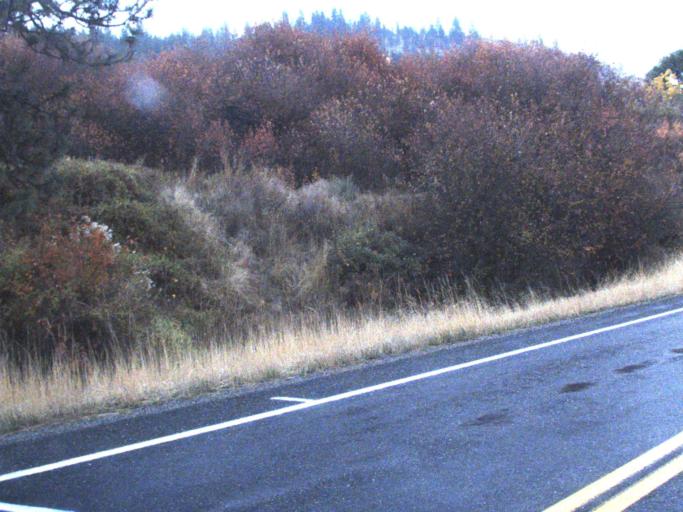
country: US
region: Washington
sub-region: Stevens County
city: Kettle Falls
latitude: 48.4780
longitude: -118.1695
